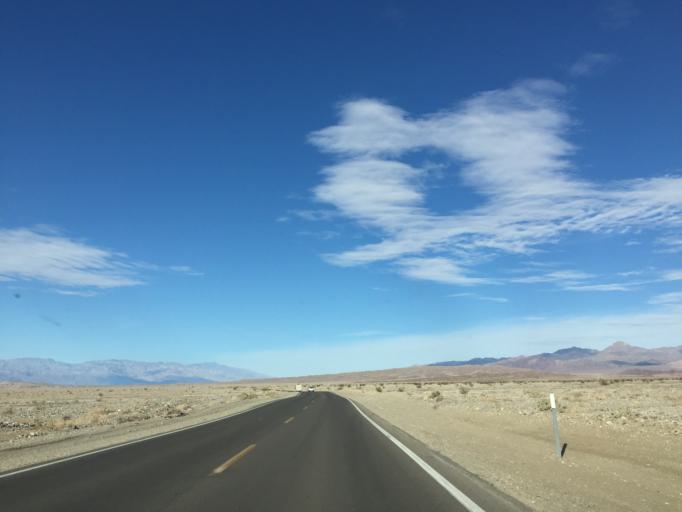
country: US
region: Nevada
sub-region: Nye County
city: Beatty
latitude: 36.5813
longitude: -116.9326
